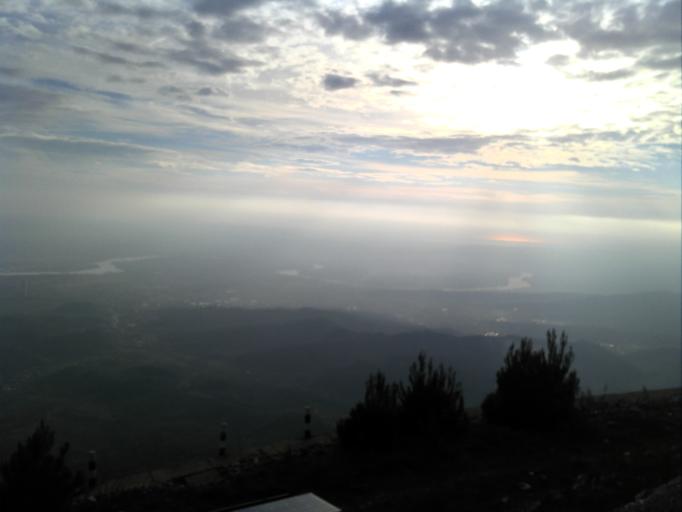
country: AL
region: Shkoder
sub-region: Rrethi i Shkodres
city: Berdica e Madhe
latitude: 42.0464
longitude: 19.4500
